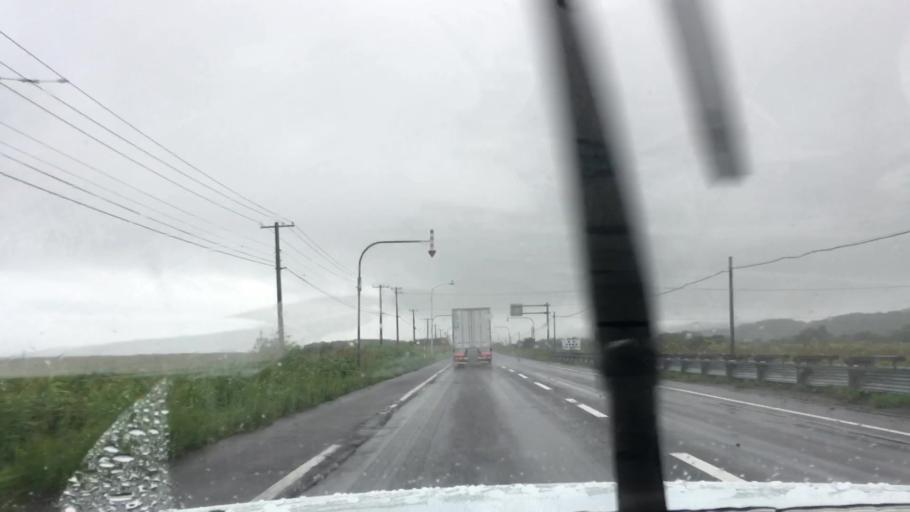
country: JP
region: Hokkaido
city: Niseko Town
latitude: 42.4249
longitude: 140.3153
